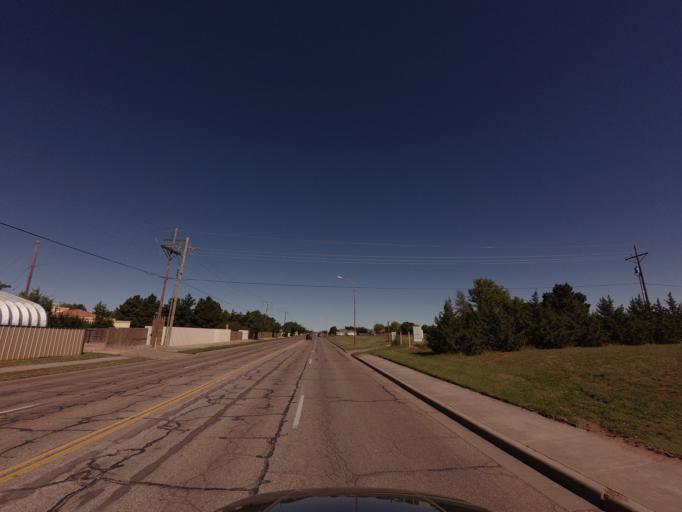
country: US
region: New Mexico
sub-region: Curry County
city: Clovis
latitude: 34.4263
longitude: -103.1785
